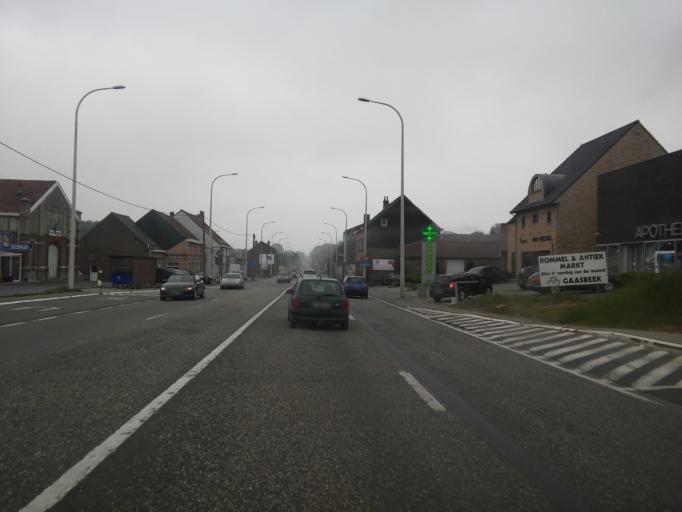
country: BE
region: Flanders
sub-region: Provincie Vlaams-Brabant
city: Lennik
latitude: 50.8350
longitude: 4.1474
